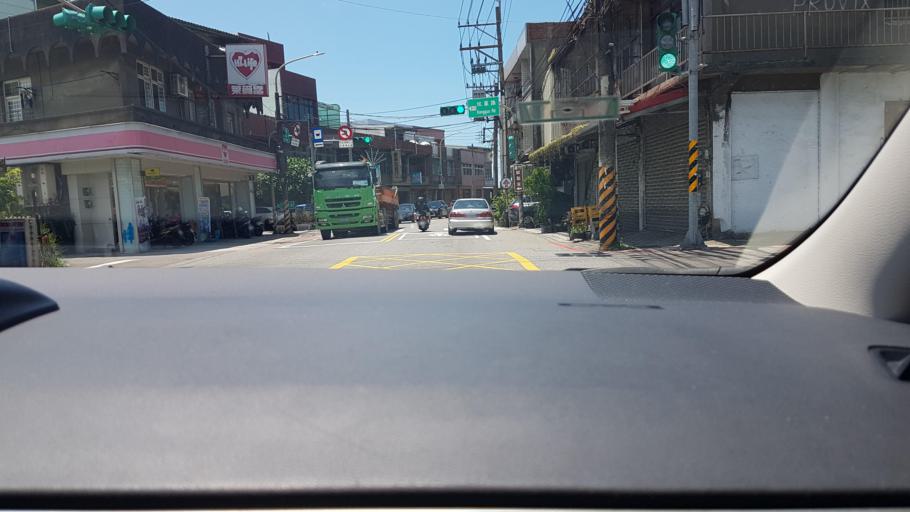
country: TW
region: Taiwan
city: Taoyuan City
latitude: 25.0921
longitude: 121.2695
